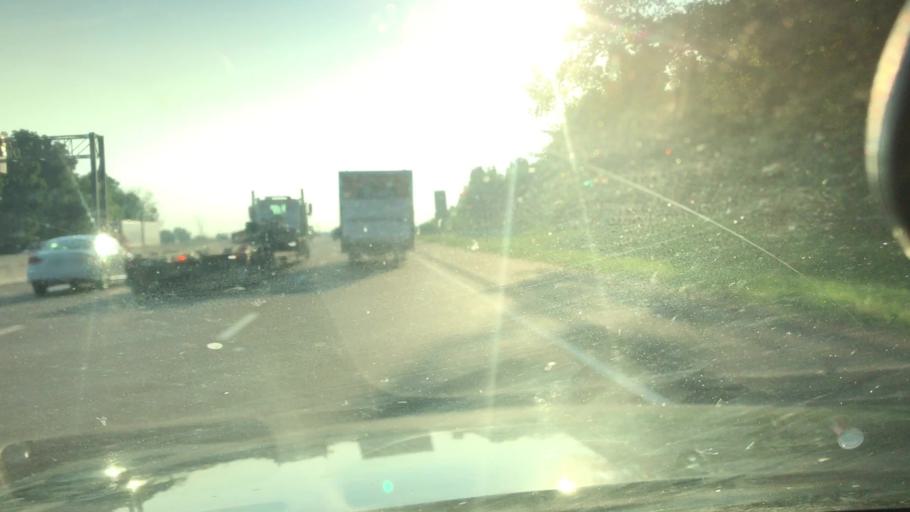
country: US
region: Tennessee
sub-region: Shelby County
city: Bartlett
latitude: 35.1799
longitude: -89.8256
